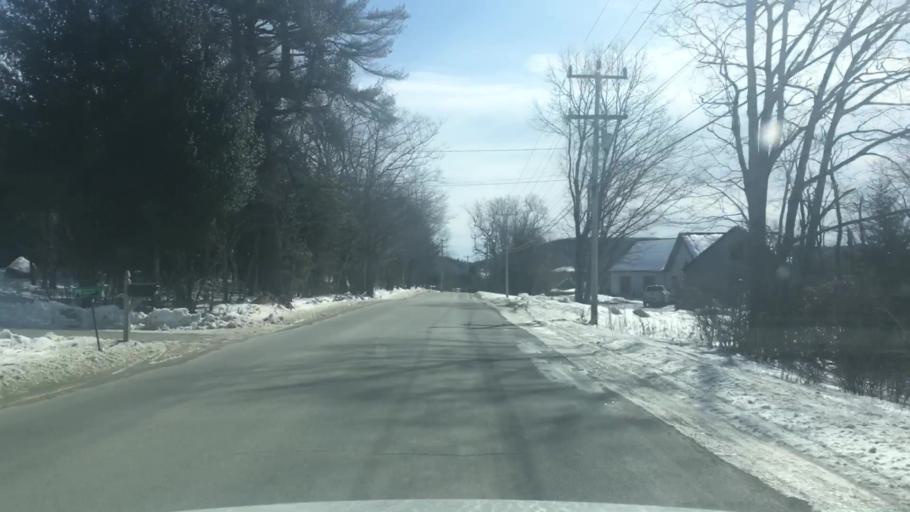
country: US
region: Maine
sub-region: Penobscot County
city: Holden
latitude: 44.7429
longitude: -68.6299
